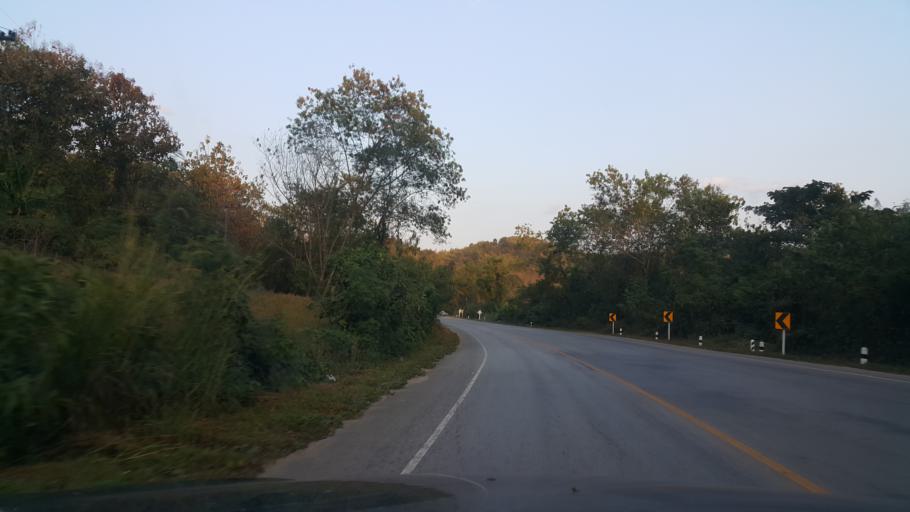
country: TH
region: Loei
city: Loei
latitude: 17.4782
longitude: 101.5543
